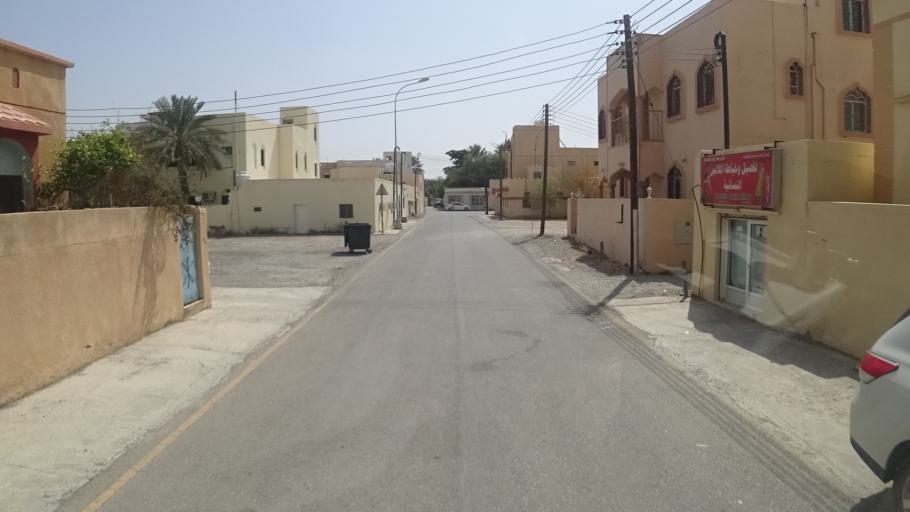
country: OM
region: Muhafazat ad Dakhiliyah
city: Bahla'
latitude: 23.1194
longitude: 57.2929
